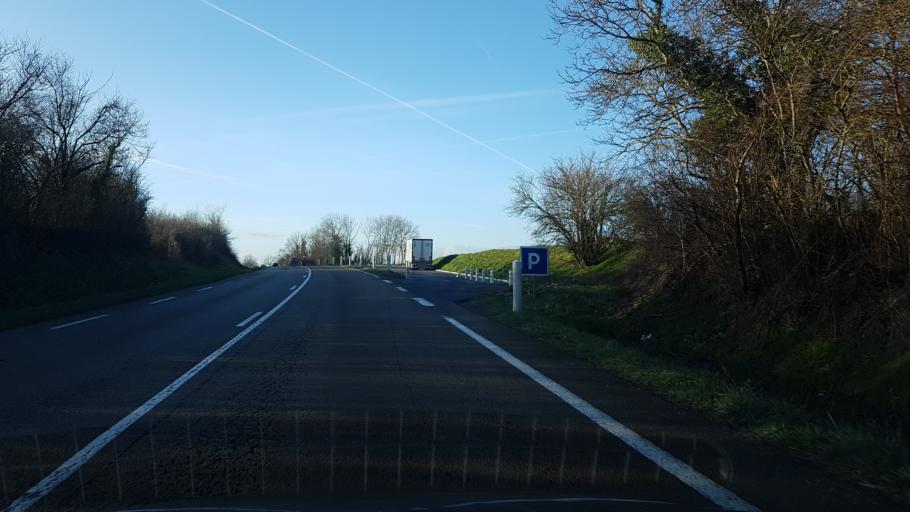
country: FR
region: Champagne-Ardenne
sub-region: Departement de la Marne
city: Vitry-le-Francois
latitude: 48.7428
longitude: 4.5278
